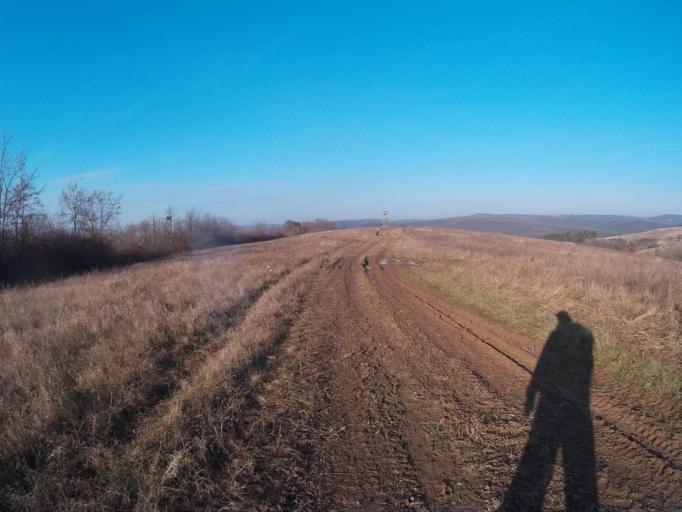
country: HU
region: Nograd
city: Bercel
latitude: 47.9675
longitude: 19.4400
